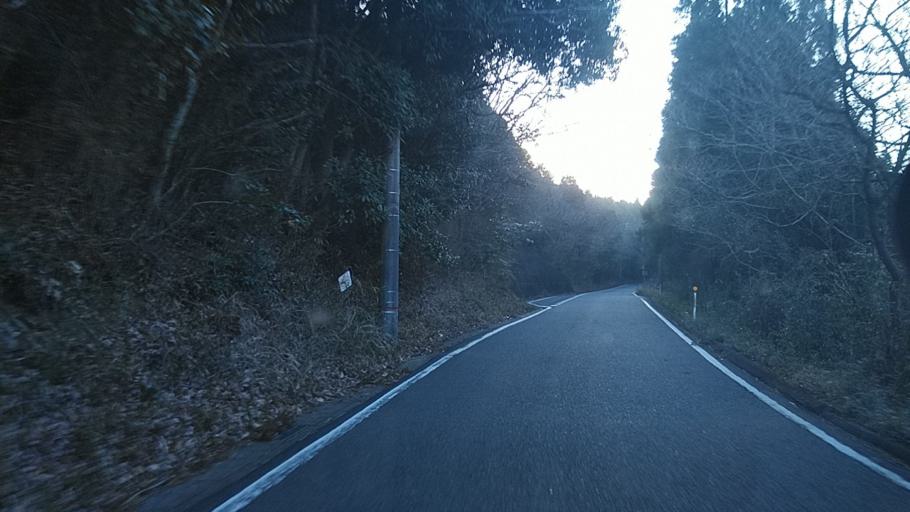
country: JP
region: Chiba
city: Kimitsu
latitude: 35.2600
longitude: 139.9443
